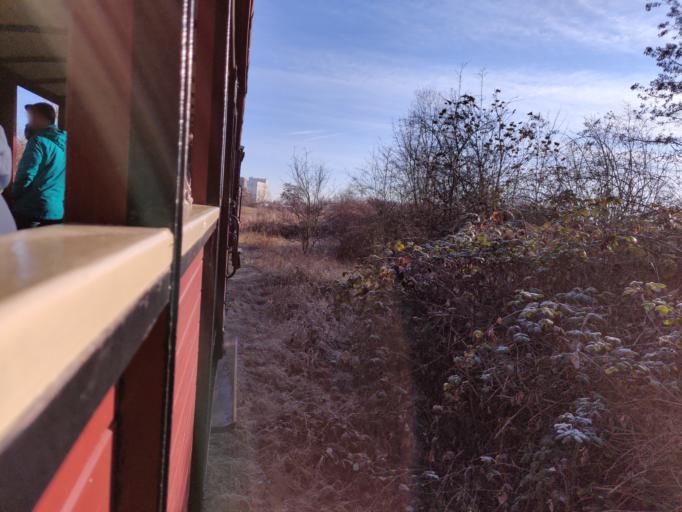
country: DE
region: Saxony
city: Markranstadt
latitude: 51.3372
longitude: 12.2895
